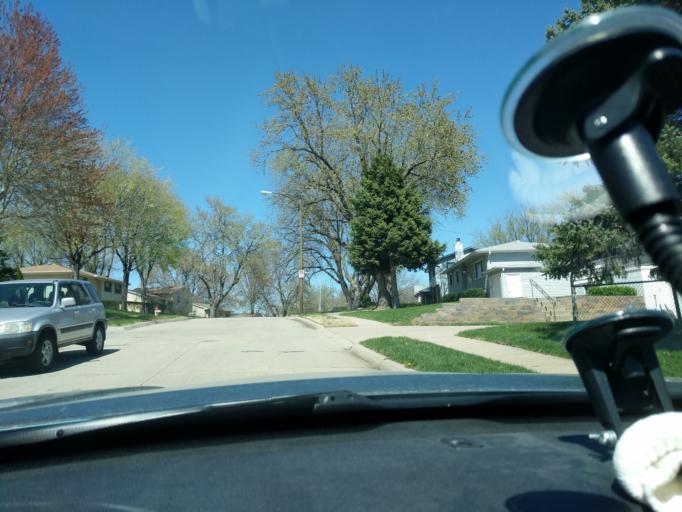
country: US
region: Nebraska
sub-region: Douglas County
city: Ralston
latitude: 41.2317
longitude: -96.0969
